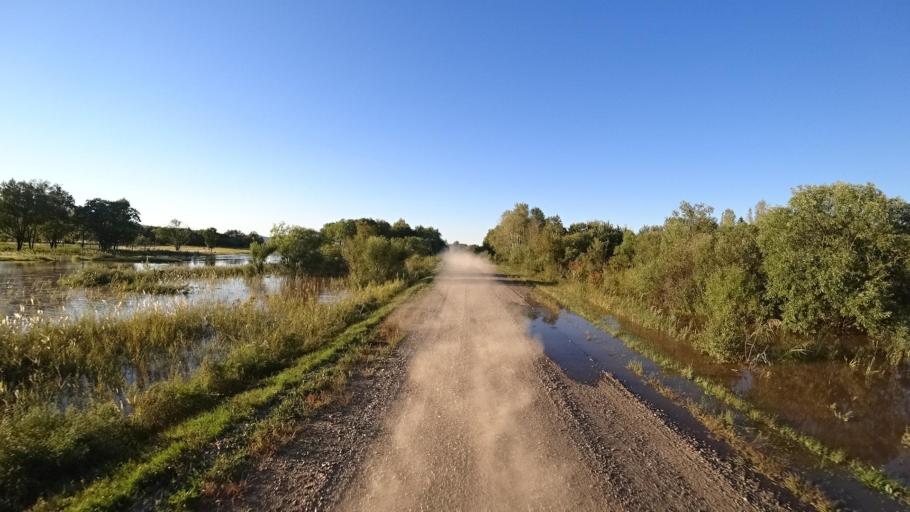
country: RU
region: Primorskiy
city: Kirovskiy
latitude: 44.7803
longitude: 133.6259
